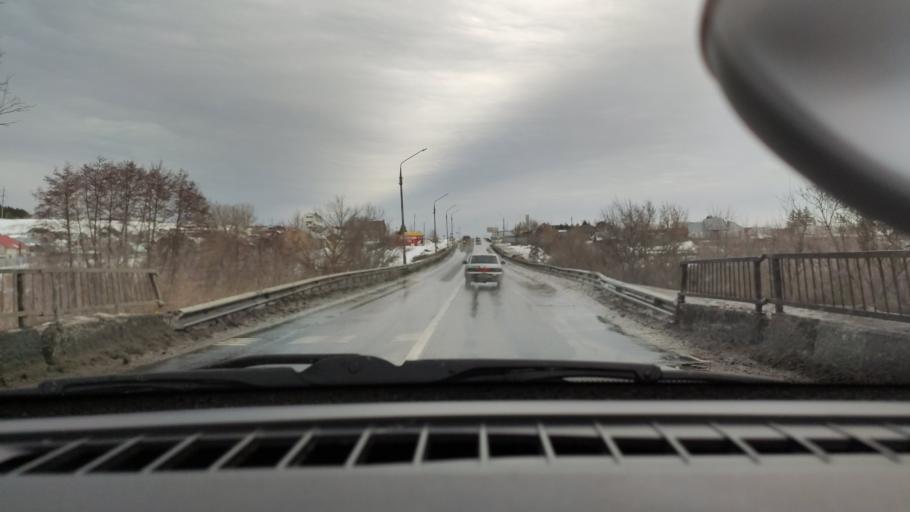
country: RU
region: Samara
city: Kurumoch
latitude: 53.4822
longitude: 50.0431
